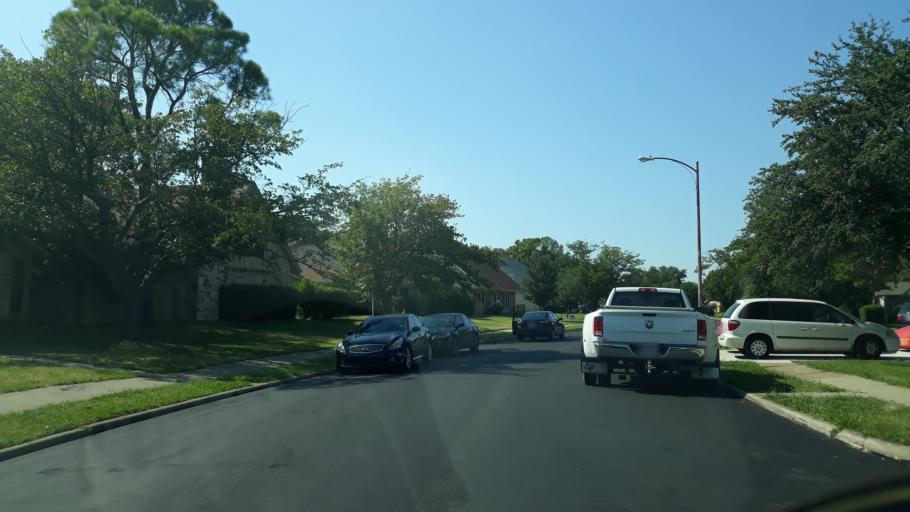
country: US
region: Texas
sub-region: Dallas County
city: Irving
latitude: 32.8453
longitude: -97.0026
